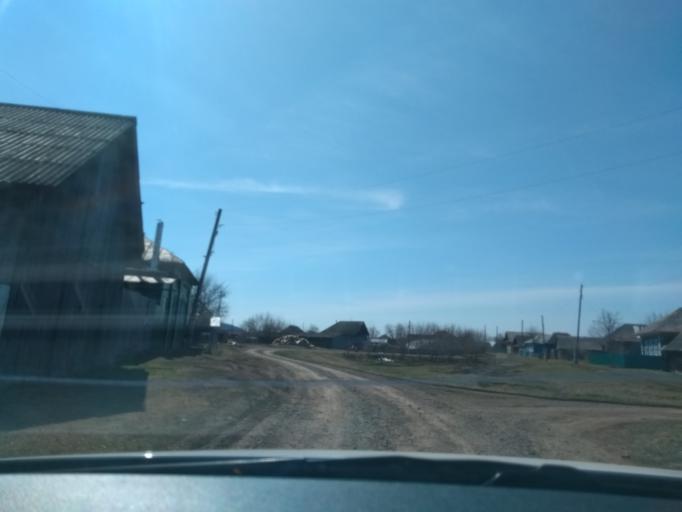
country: RU
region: Perm
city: Orda
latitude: 57.2180
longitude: 56.5994
